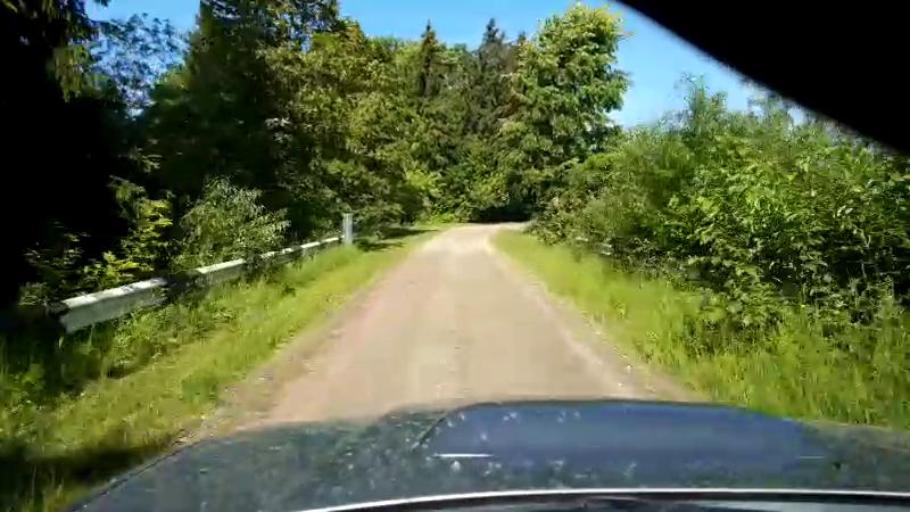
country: EE
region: Paernumaa
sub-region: Sindi linn
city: Sindi
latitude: 58.5170
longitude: 24.6604
